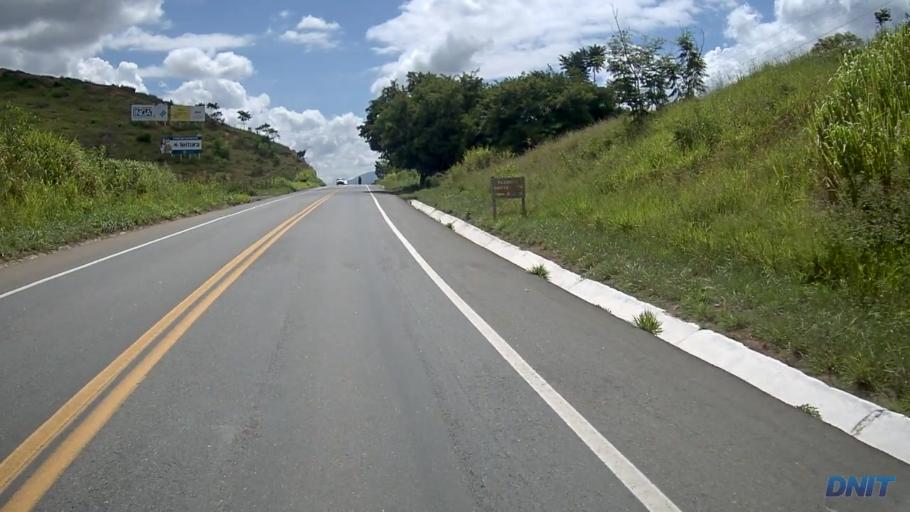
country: BR
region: Minas Gerais
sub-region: Governador Valadares
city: Governador Valadares
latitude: -18.9438
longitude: -42.0634
